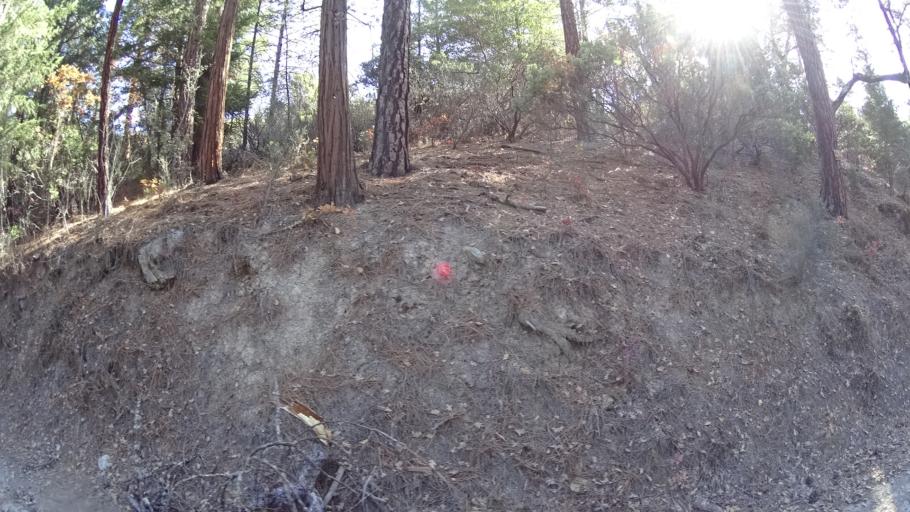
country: US
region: California
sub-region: Siskiyou County
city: Yreka
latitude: 41.8517
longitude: -122.8336
